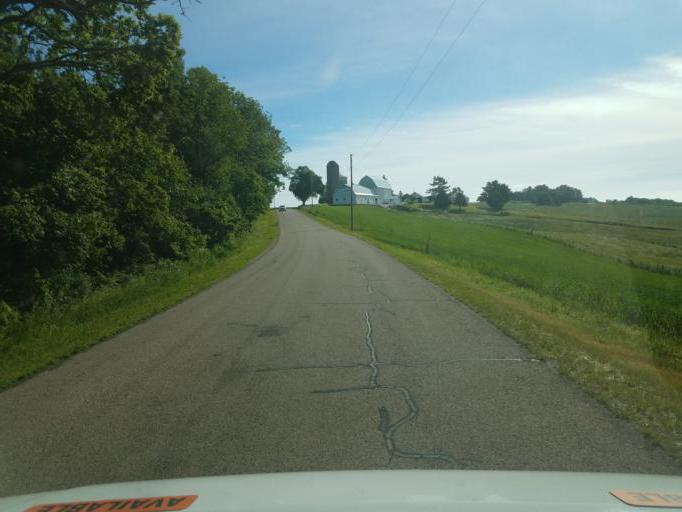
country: US
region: Wisconsin
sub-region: Sauk County
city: Reedsburg
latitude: 43.5387
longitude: -90.0760
